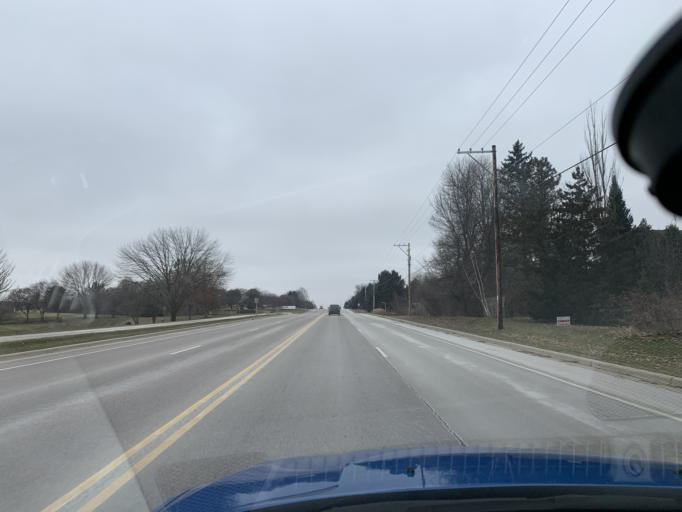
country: US
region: Wisconsin
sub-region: Dane County
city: Sun Prairie
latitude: 43.1939
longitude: -89.2642
